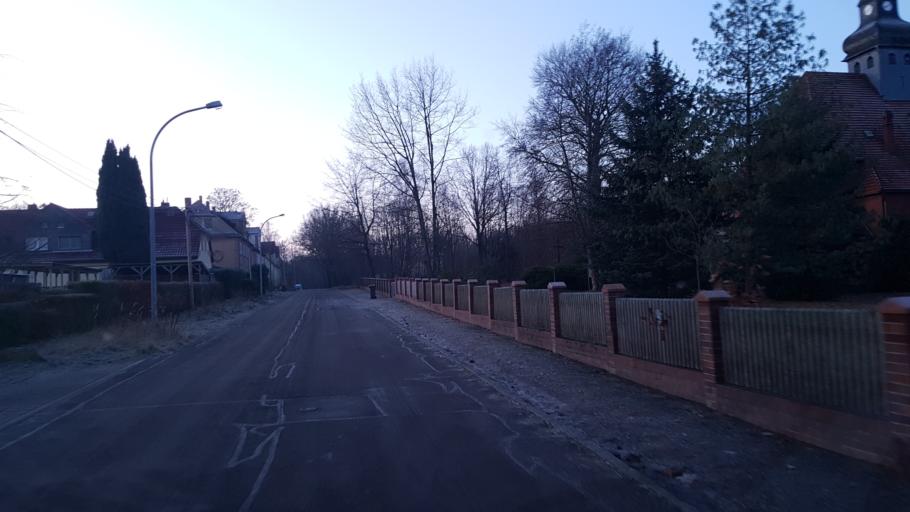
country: DE
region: Brandenburg
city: Schipkau
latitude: 51.5511
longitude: 13.8859
